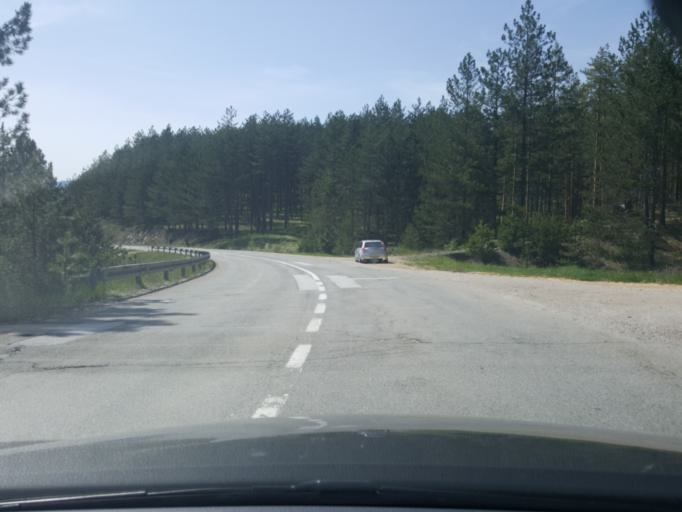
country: RS
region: Central Serbia
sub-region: Zlatiborski Okrug
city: Cajetina
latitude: 43.8333
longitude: 19.6383
